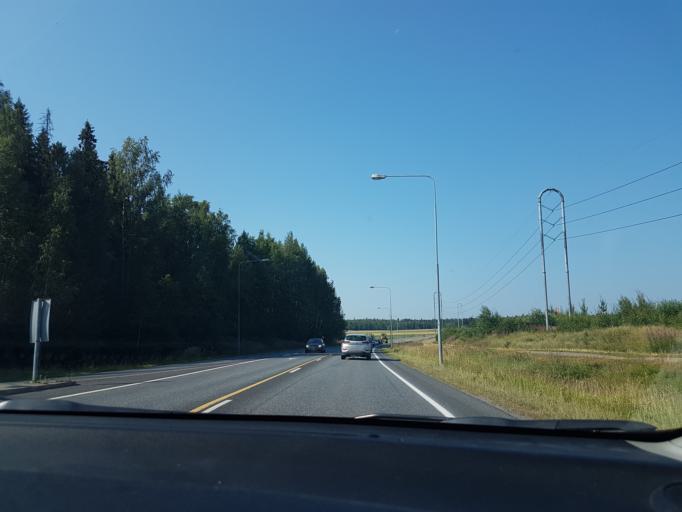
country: FI
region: Uusimaa
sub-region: Helsinki
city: Tuusula
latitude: 60.3766
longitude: 25.0528
